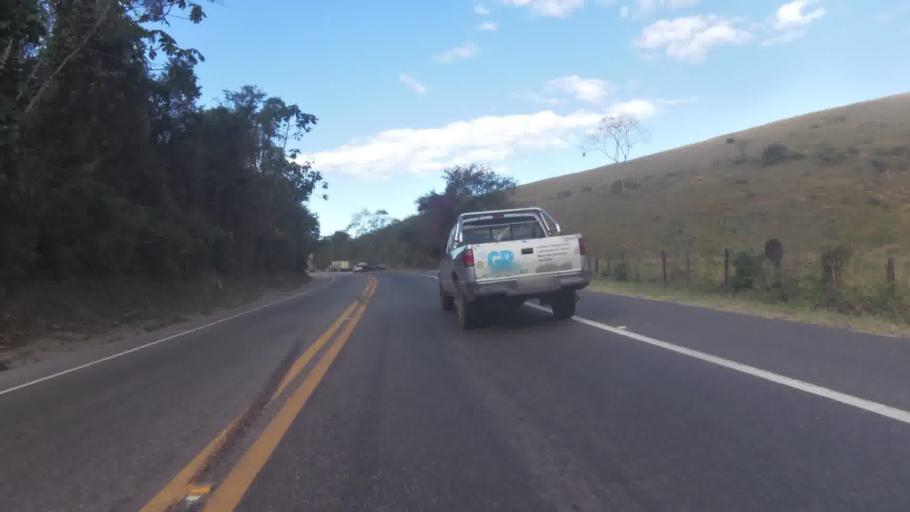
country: BR
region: Espirito Santo
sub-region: Rio Novo Do Sul
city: Rio Novo do Sul
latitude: -20.8663
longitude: -40.8897
